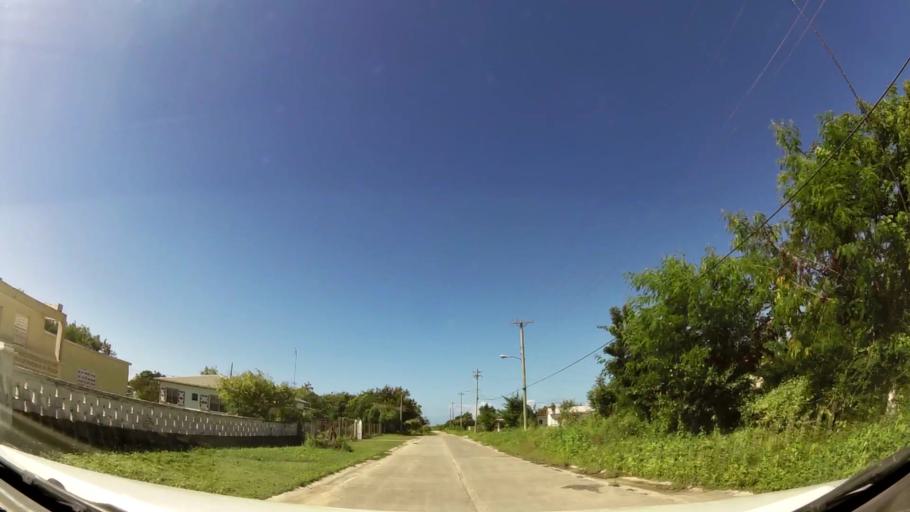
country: AG
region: Barbuda
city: Codrington
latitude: 17.6390
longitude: -61.8273
